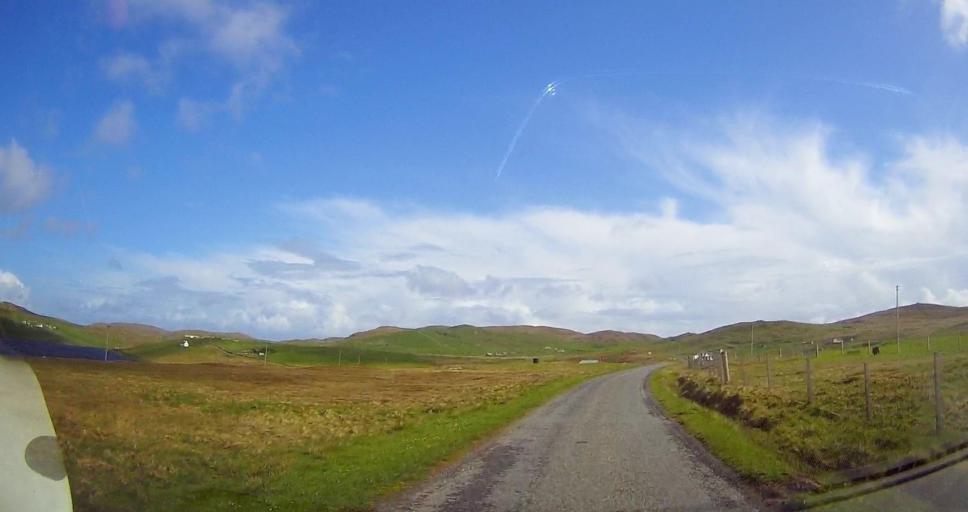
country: GB
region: Scotland
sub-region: Shetland Islands
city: Lerwick
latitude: 60.5896
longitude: -1.3333
